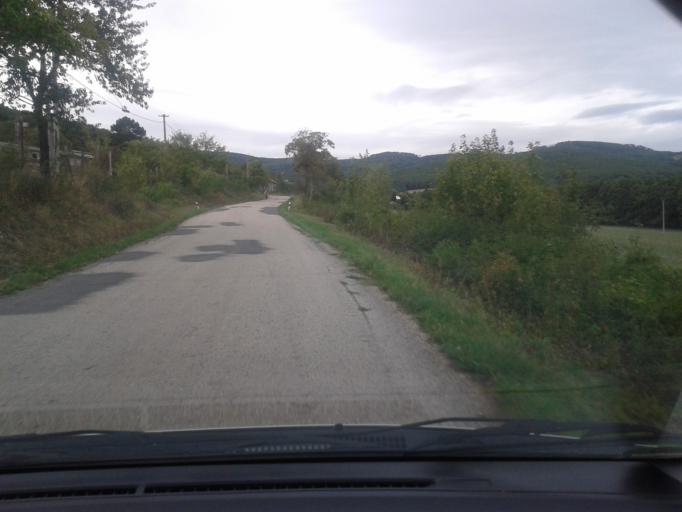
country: SK
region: Nitriansky
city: Zlate Moravce
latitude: 48.4554
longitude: 18.3206
